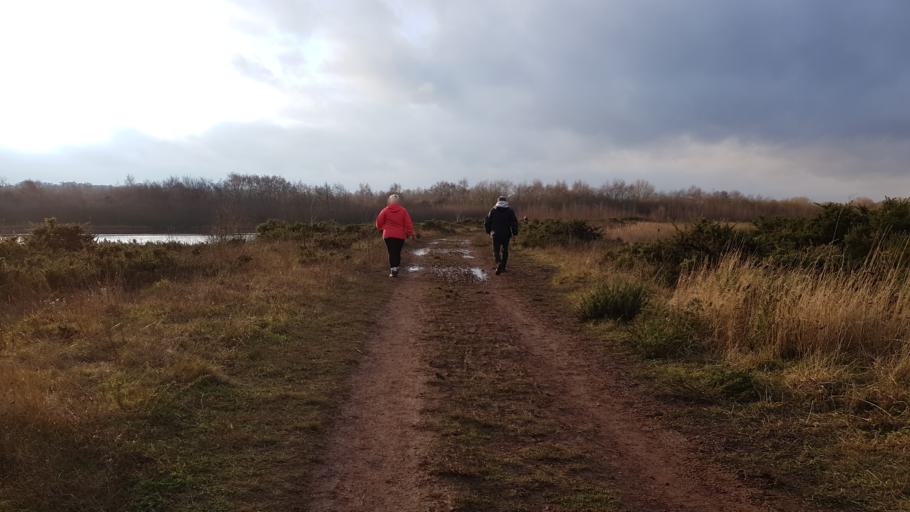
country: GB
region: England
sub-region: City and Borough of Leeds
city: Swillington
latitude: 53.7460
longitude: -1.4138
